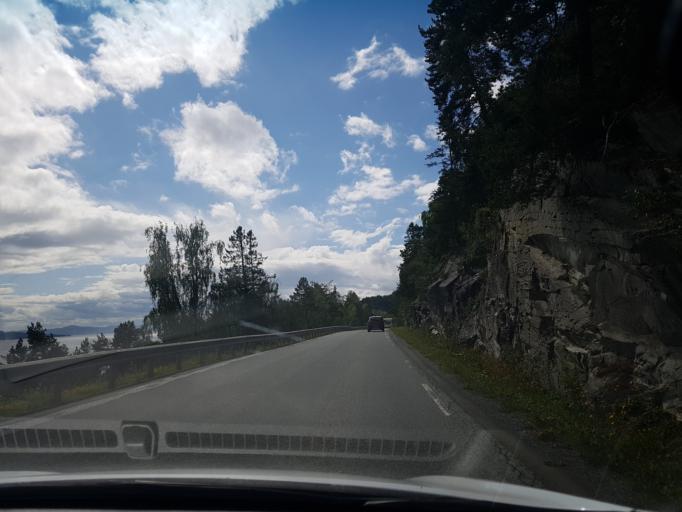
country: NO
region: Nord-Trondelag
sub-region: Frosta
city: Frosta
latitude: 63.6017
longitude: 10.8688
